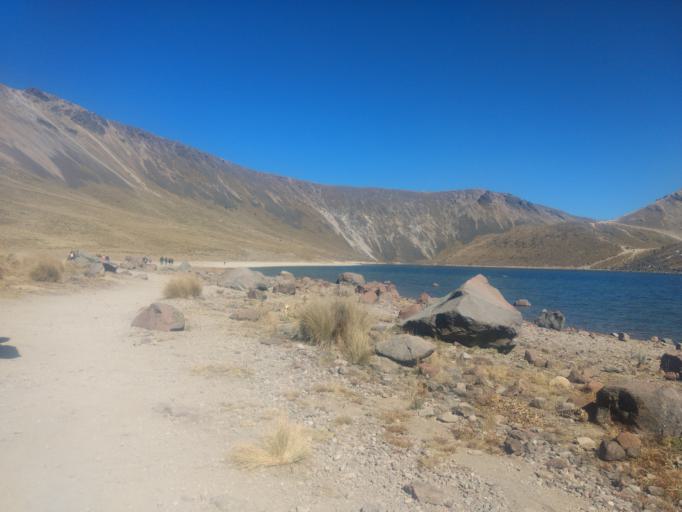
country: MX
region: Mexico
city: Cerro La Calera
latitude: 19.1092
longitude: -99.7623
